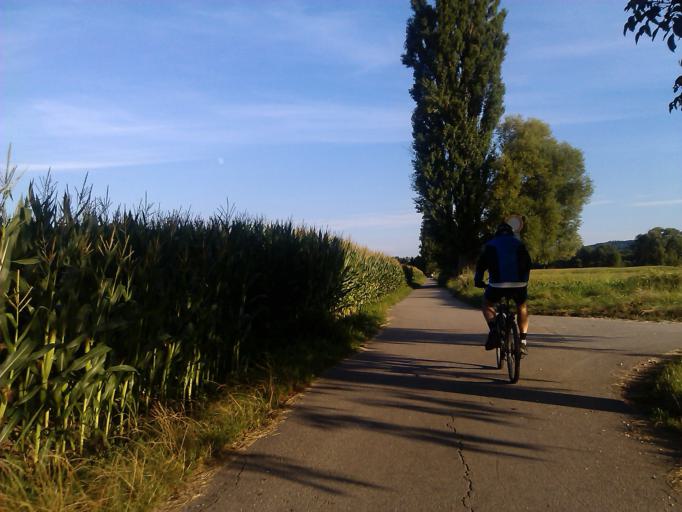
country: DE
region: Baden-Wuerttemberg
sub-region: Karlsruhe Region
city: Wiesloch
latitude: 49.2823
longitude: 8.6938
